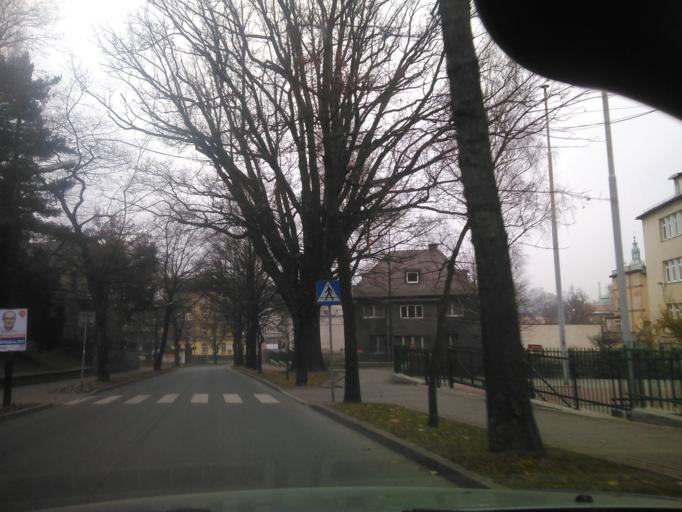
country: PL
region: Lower Silesian Voivodeship
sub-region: Jelenia Gora
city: Jelenia Gora
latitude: 50.9007
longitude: 15.7460
